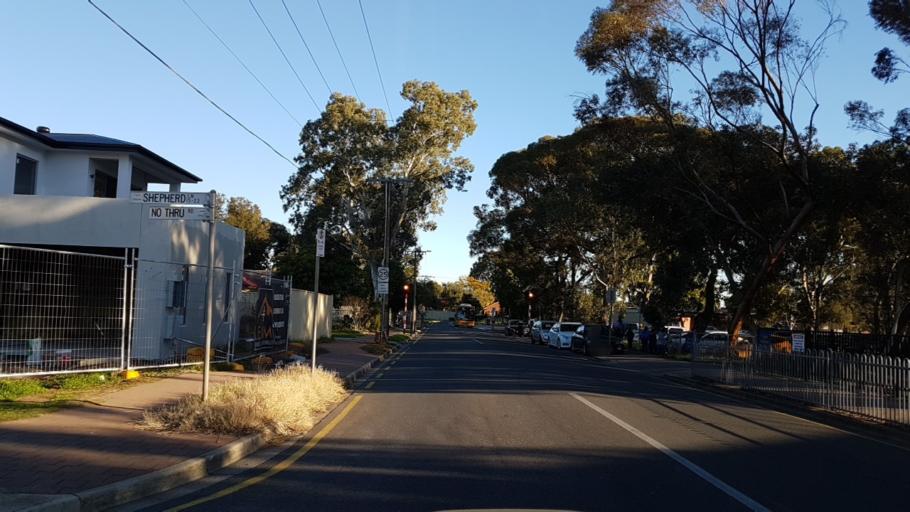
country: AU
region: South Australia
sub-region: Campbelltown
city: Hectorville
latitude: -34.8823
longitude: 138.6548
